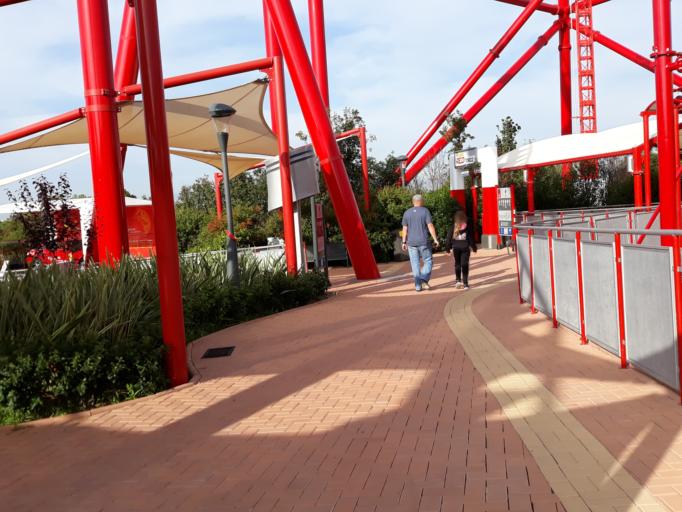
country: ES
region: Catalonia
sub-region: Provincia de Tarragona
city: Salou
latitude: 41.0844
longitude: 1.1506
